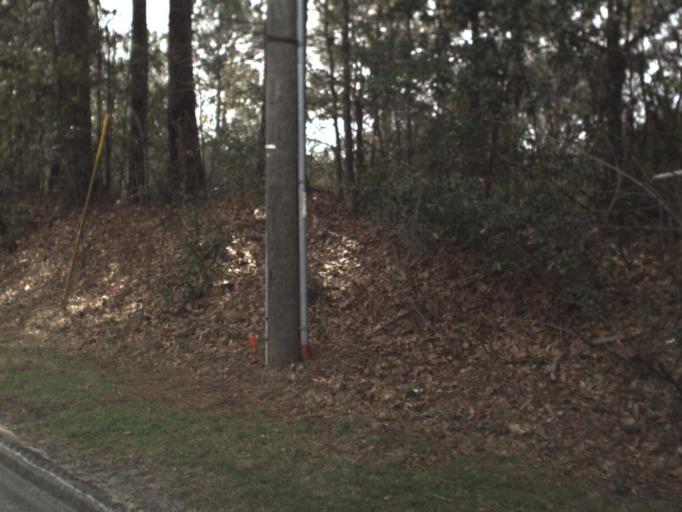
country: US
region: Florida
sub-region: Washington County
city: Chipley
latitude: 30.6918
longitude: -85.3924
